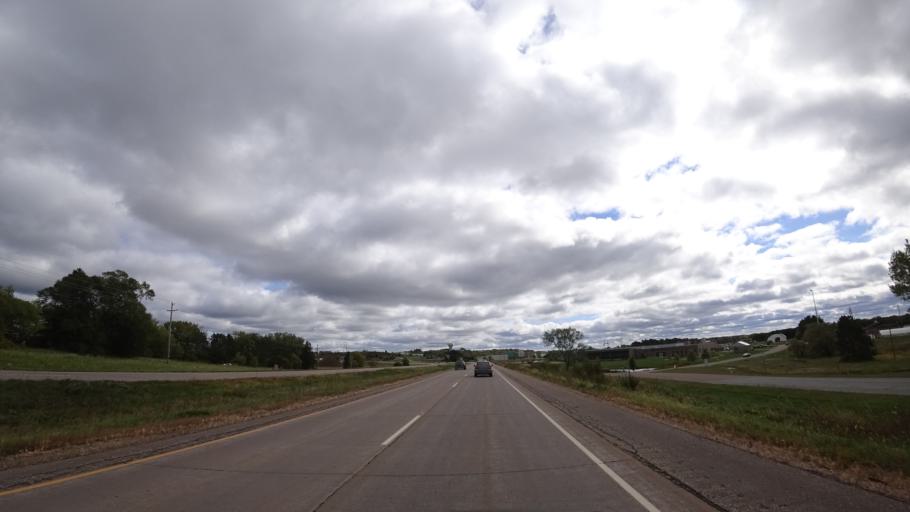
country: US
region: Wisconsin
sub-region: Eau Claire County
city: Eau Claire
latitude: 44.8404
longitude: -91.5538
